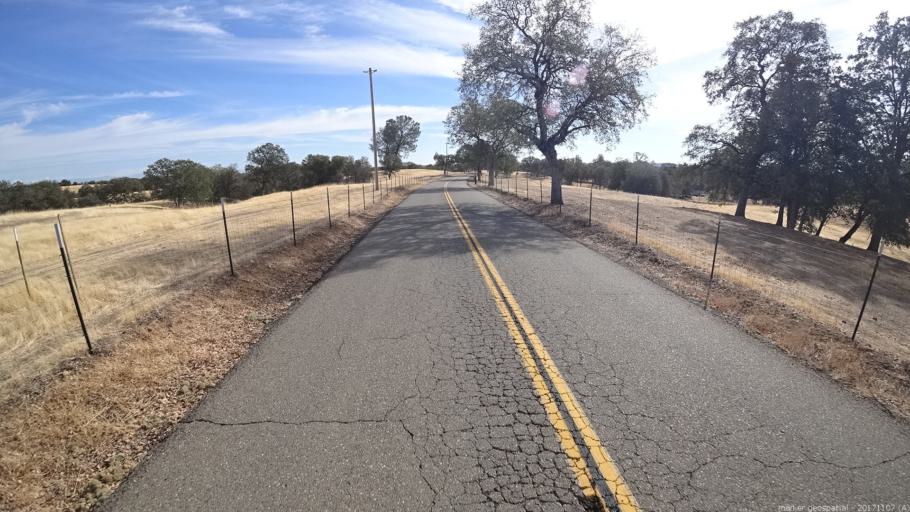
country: US
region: California
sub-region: Shasta County
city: Shasta
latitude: 40.4330
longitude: -122.5222
